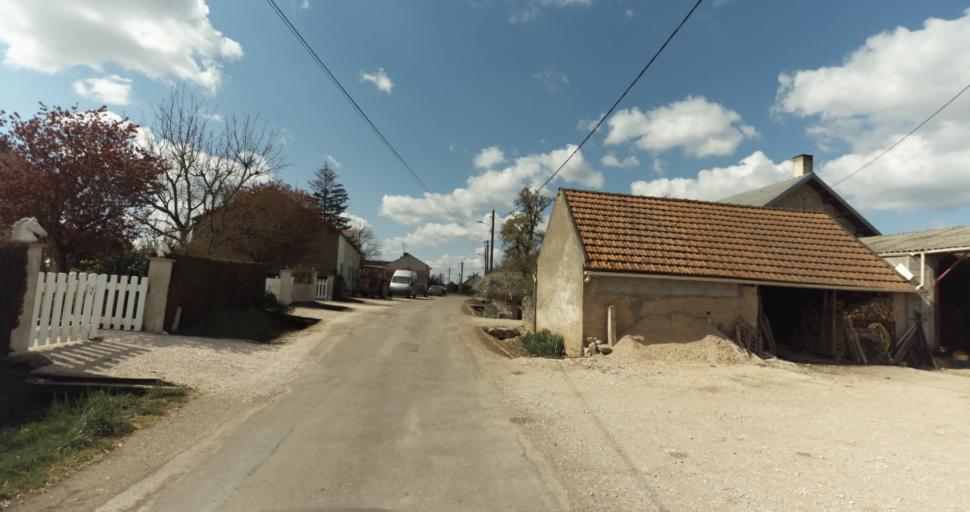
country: FR
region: Bourgogne
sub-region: Departement de la Cote-d'Or
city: Auxonne
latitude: 47.2082
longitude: 5.4095
